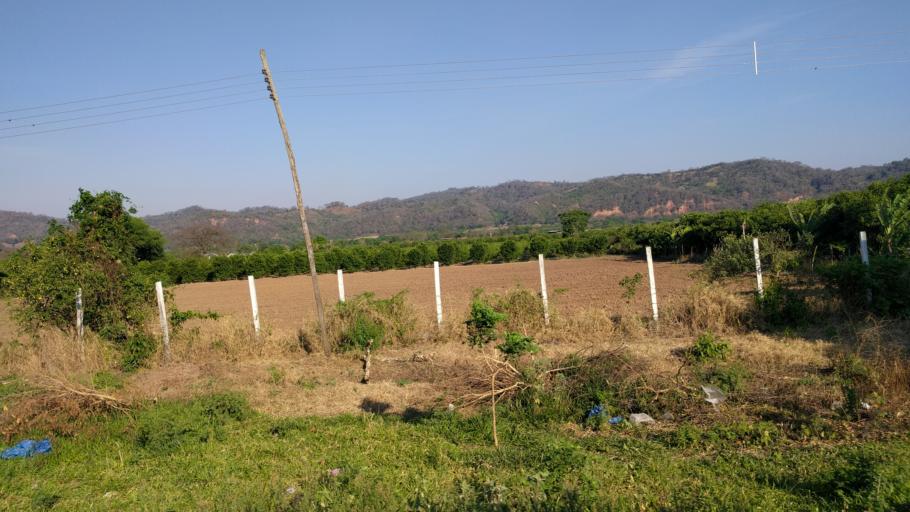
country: BO
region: Santa Cruz
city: Jorochito
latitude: -18.1341
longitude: -63.4727
